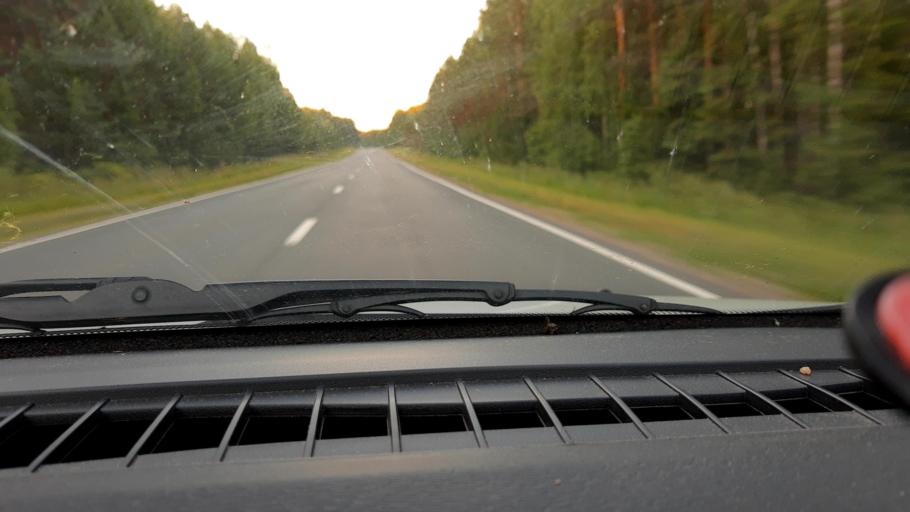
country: RU
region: Nizjnij Novgorod
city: Krasnyye Baki
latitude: 57.1987
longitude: 45.4476
